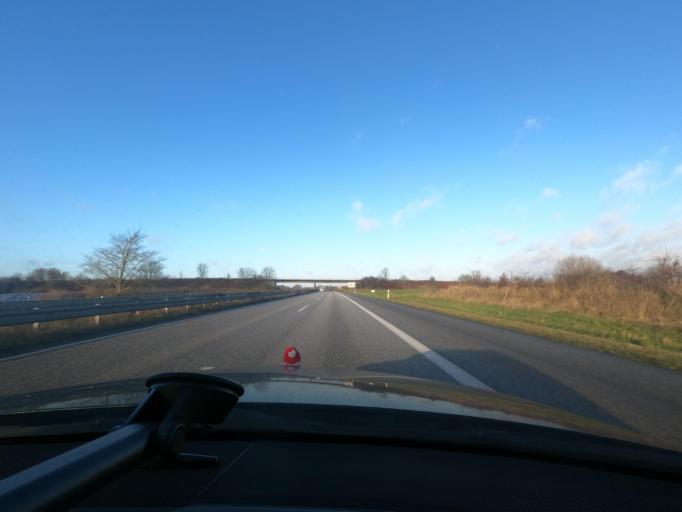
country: DE
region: Schleswig-Holstein
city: Sankelmark
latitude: 54.7174
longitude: 9.3995
